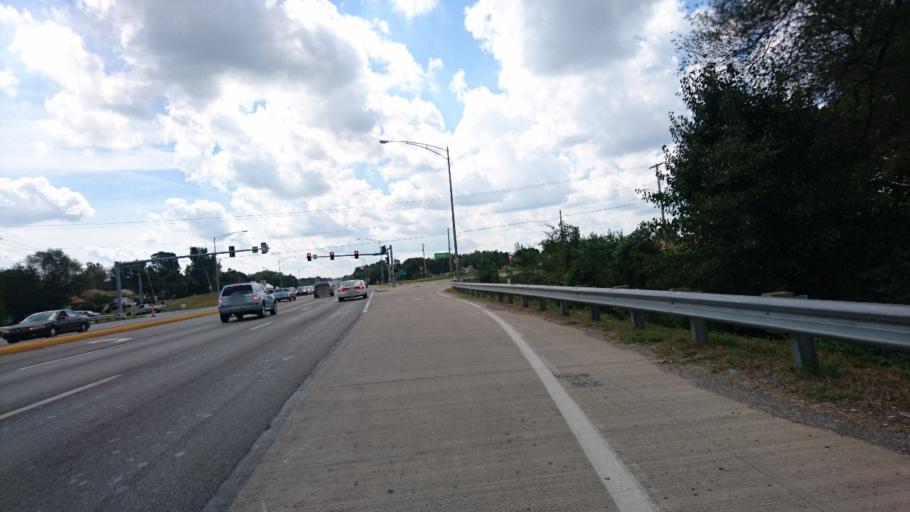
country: US
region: Missouri
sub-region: Greene County
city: Springfield
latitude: 37.2057
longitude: -93.3495
